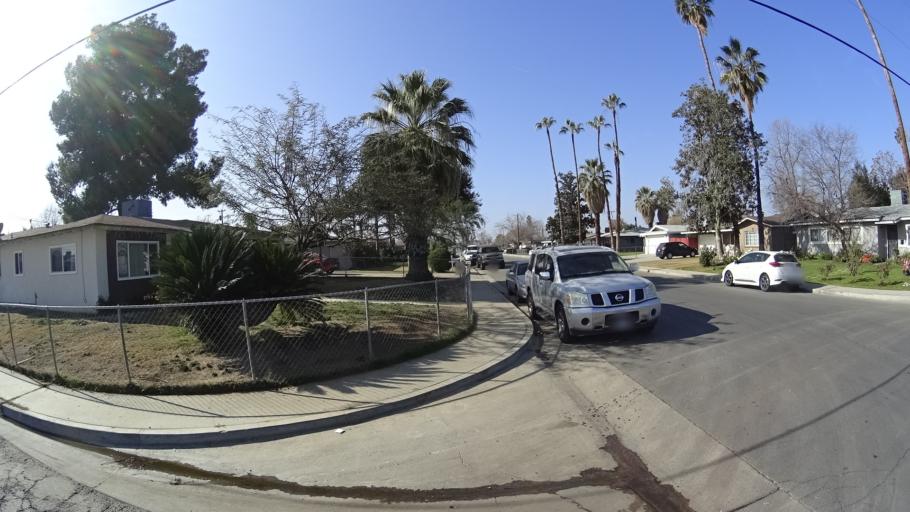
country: US
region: California
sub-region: Kern County
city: Bakersfield
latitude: 35.3346
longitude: -119.0455
